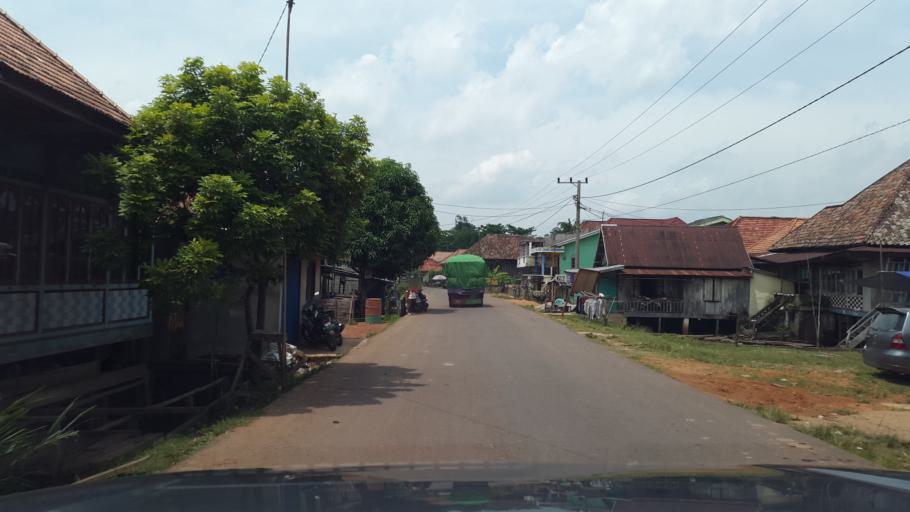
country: ID
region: South Sumatra
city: Tanjung Lubuk
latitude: -3.1723
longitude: 104.8705
